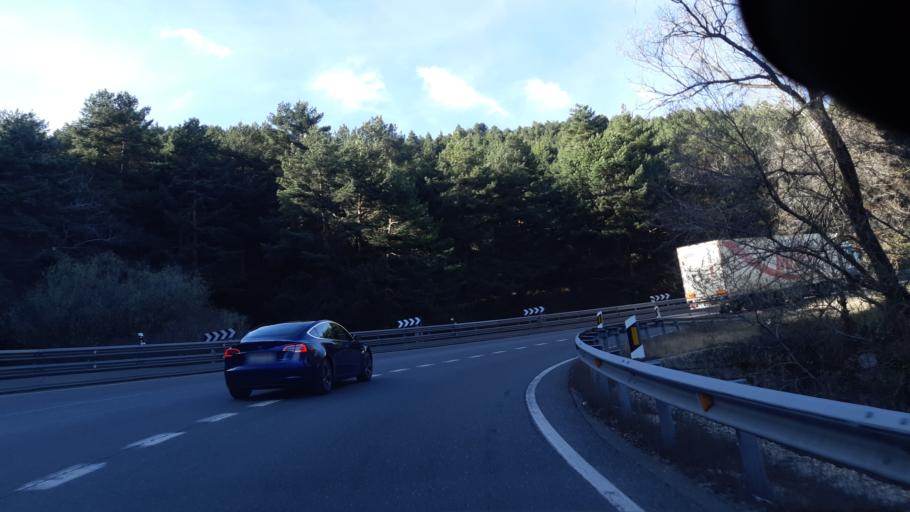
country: ES
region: Madrid
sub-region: Provincia de Madrid
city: Guadarrama
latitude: 40.6989
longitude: -4.1310
